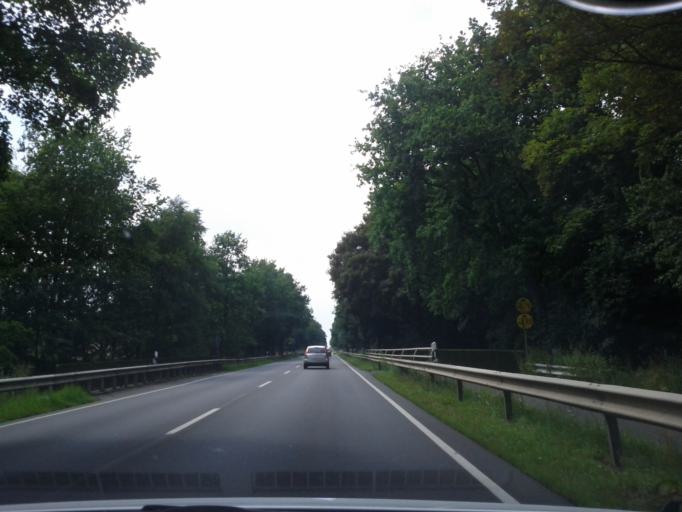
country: DE
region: Lower Saxony
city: Stade
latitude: 53.5827
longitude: 9.4860
